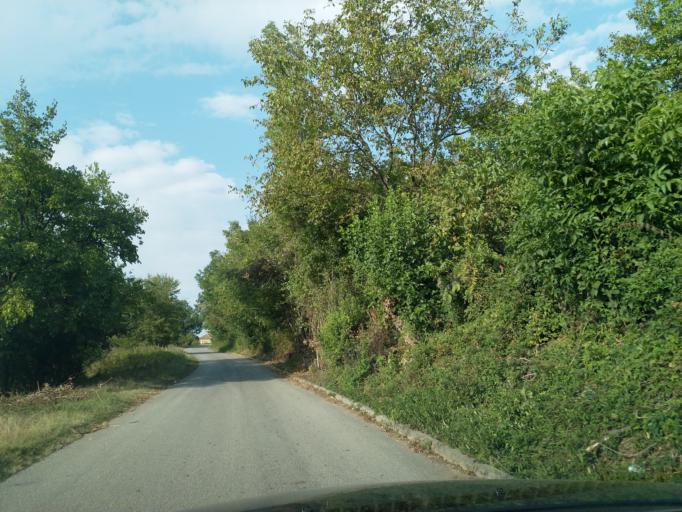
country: RS
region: Central Serbia
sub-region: Pomoravski Okrug
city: Paracin
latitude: 43.8480
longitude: 21.5280
